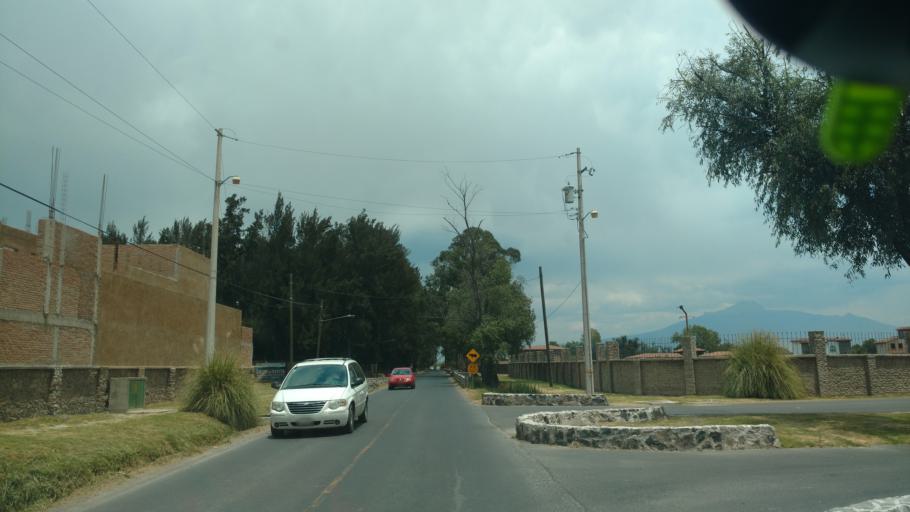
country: MX
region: Puebla
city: San Miguel Xoxtla
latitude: 19.1881
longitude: -98.2930
